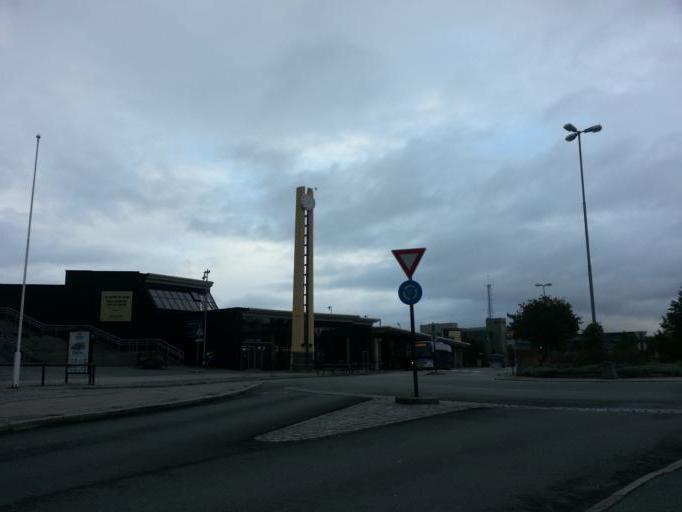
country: NO
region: Sor-Trondelag
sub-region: Trondheim
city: Trondheim
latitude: 63.4359
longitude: 10.3994
